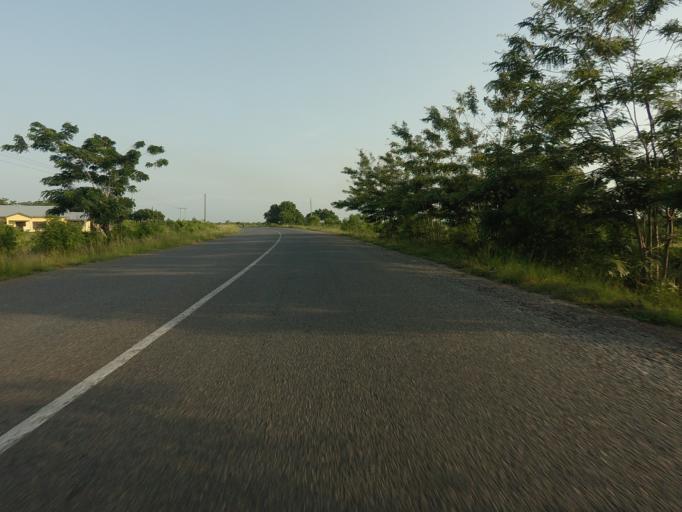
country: GH
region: Volta
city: Anloga
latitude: 5.9680
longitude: 0.6619
